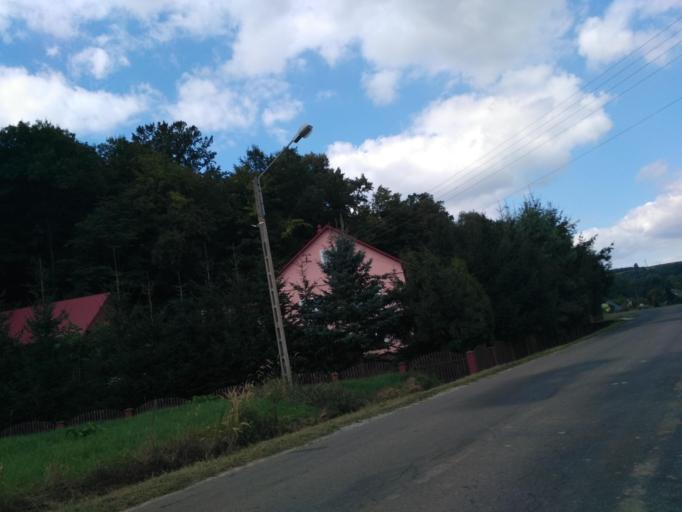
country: PL
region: Subcarpathian Voivodeship
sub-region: Powiat brzozowski
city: Nozdrzec
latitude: 49.7837
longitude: 22.2126
